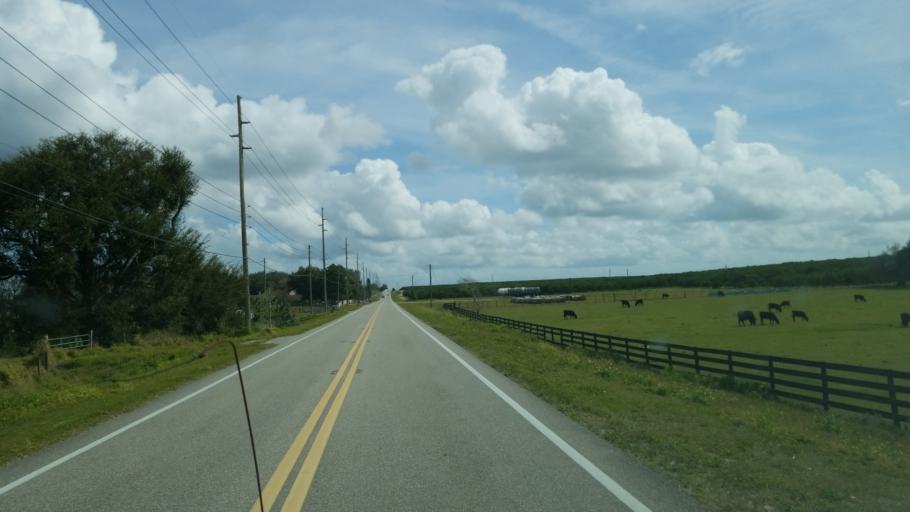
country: US
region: Florida
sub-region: Polk County
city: Dundee
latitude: 28.0409
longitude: -81.5804
